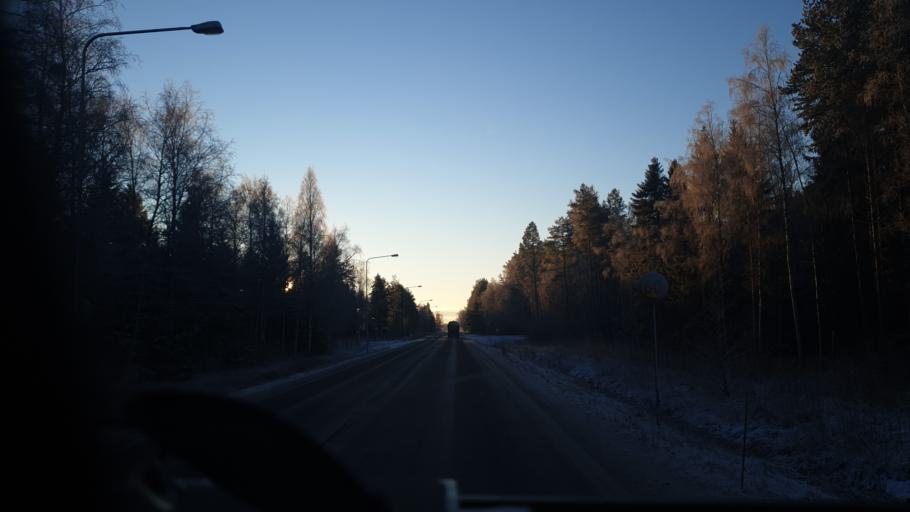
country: FI
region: Northern Ostrobothnia
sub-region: Ylivieska
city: Kalajoki
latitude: 64.2737
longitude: 23.9489
